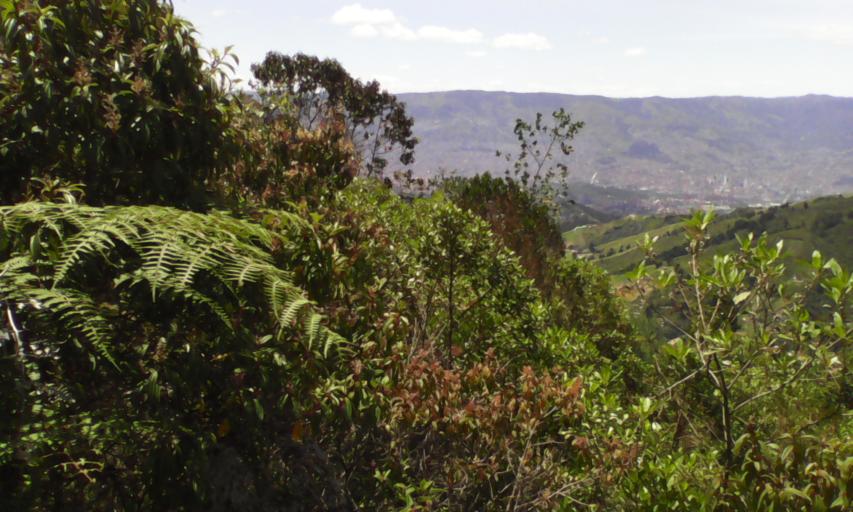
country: CO
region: Antioquia
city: Heliconia
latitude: 6.2727
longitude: -75.6672
